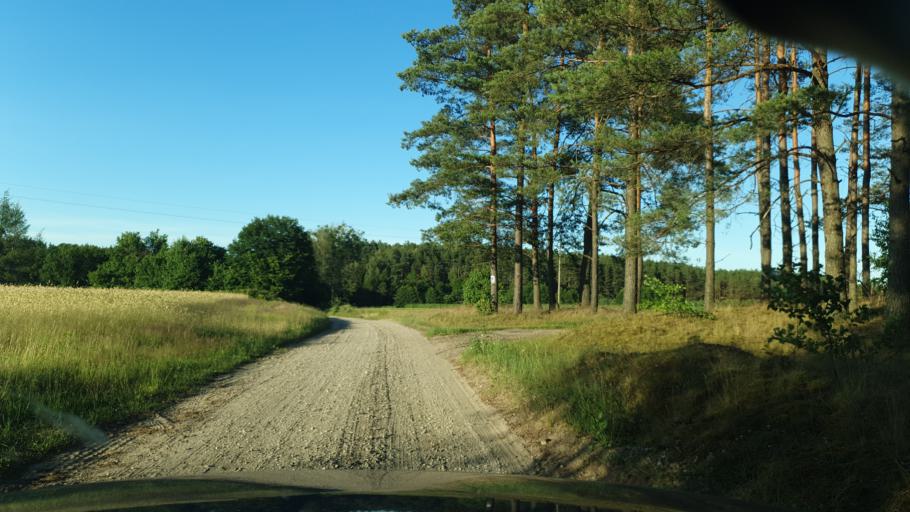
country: PL
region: Pomeranian Voivodeship
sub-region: Powiat bytowski
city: Lipnica
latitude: 53.8769
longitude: 17.4222
